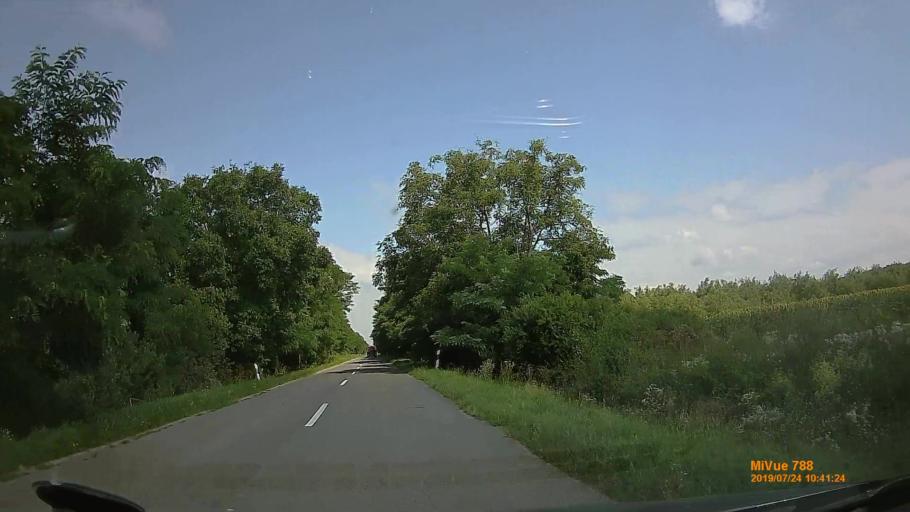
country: HU
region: Szabolcs-Szatmar-Bereg
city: Tarpa
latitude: 48.1873
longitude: 22.5486
